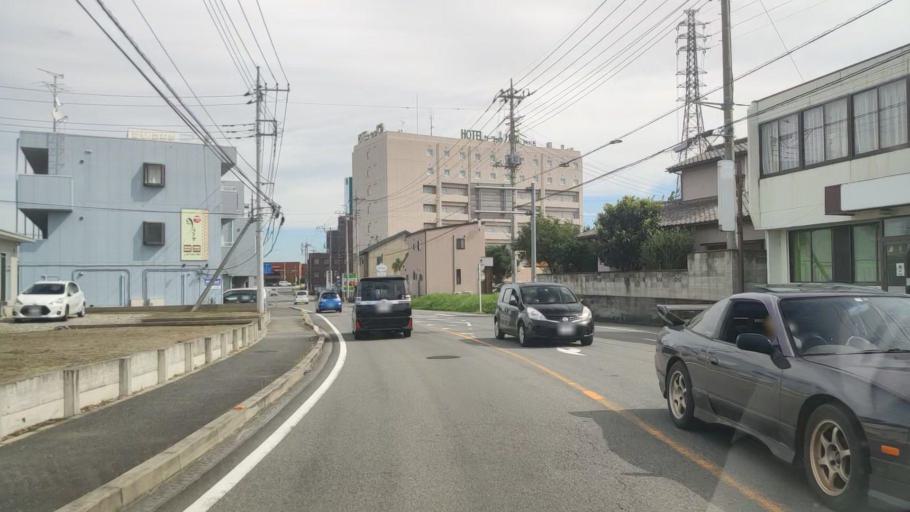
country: JP
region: Gunma
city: Takasaki
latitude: 36.3586
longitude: 139.0125
